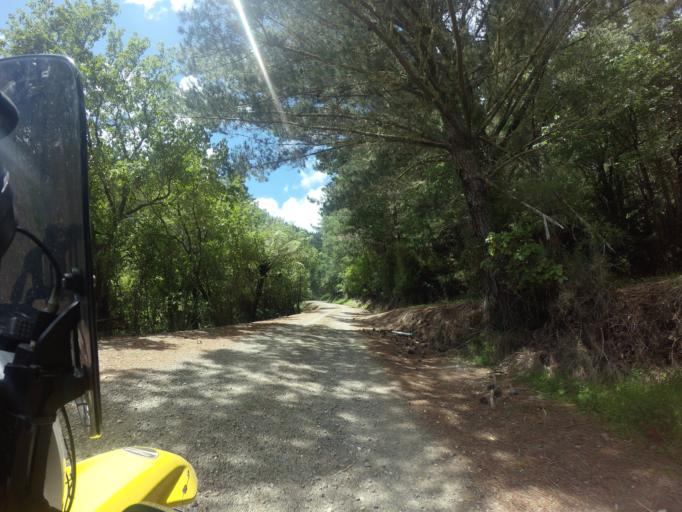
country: NZ
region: Hawke's Bay
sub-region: Wairoa District
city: Wairoa
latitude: -38.9716
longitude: 177.6823
